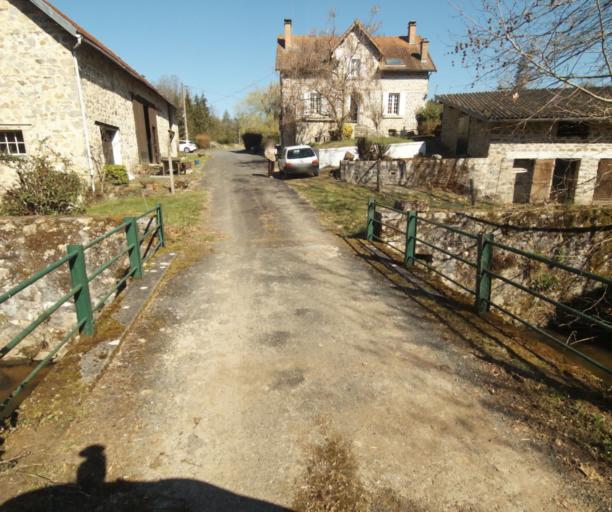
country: FR
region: Limousin
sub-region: Departement de la Correze
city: Saint-Mexant
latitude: 45.2920
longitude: 1.6132
